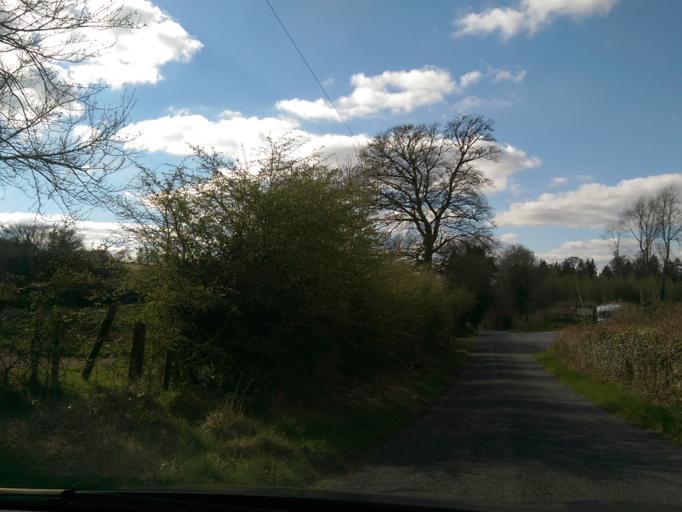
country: IE
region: Munster
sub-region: North Tipperary
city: Roscrea
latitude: 53.0913
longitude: -7.6839
